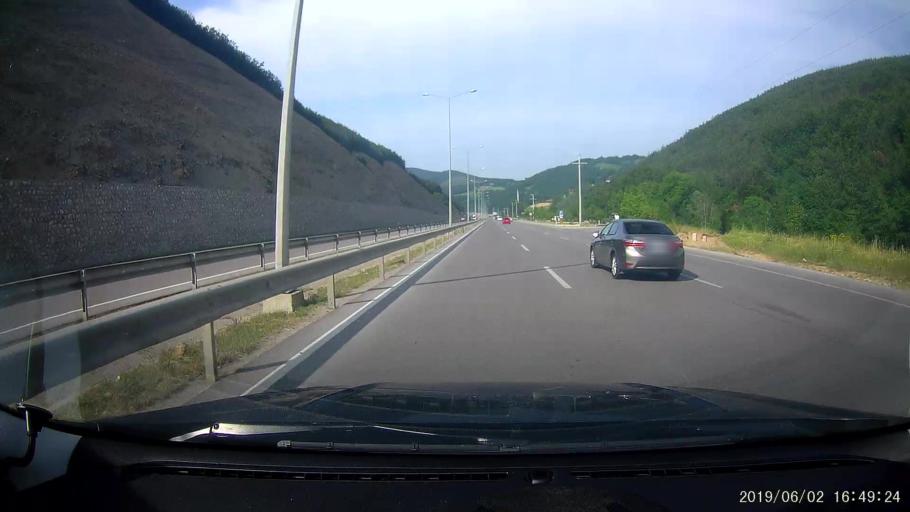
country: TR
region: Samsun
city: Taflan
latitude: 41.2370
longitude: 36.1609
